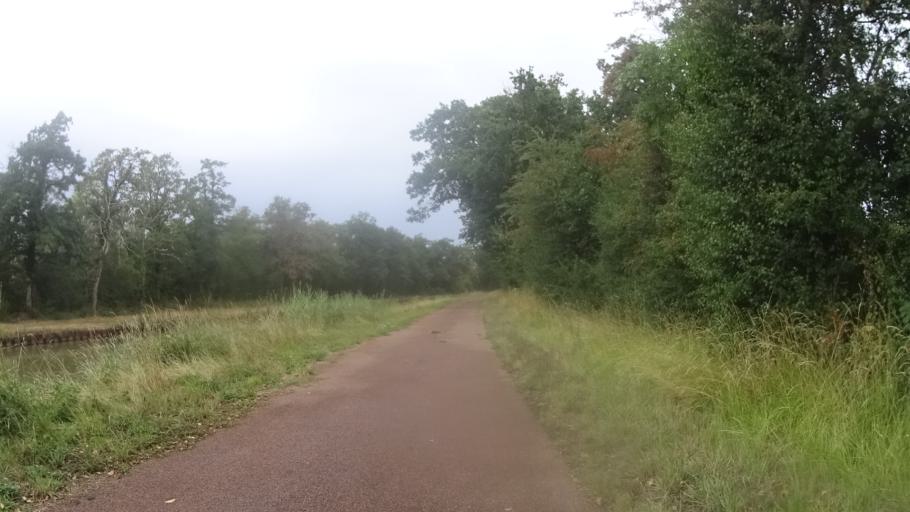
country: FR
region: Bourgogne
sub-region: Departement de la Nievre
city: Imphy
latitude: 46.9020
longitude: 3.2458
